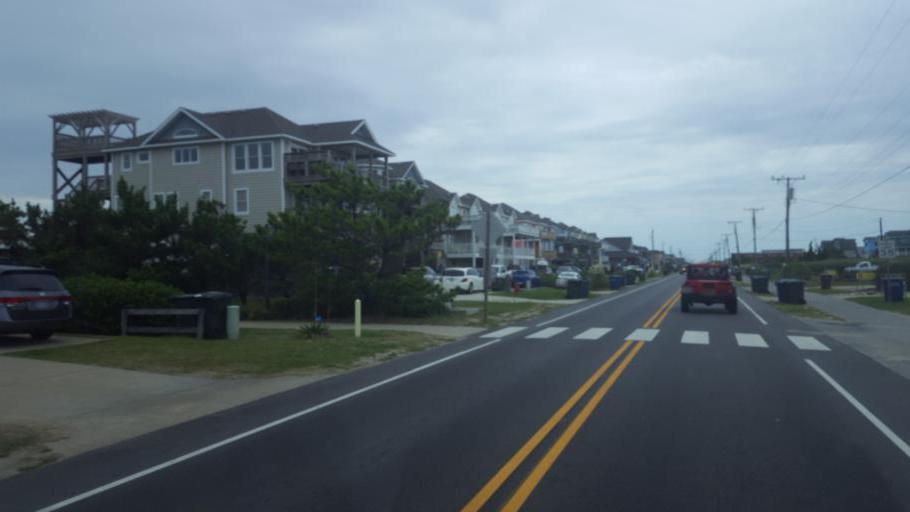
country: US
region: North Carolina
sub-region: Dare County
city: Nags Head
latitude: 35.9705
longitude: -75.6316
